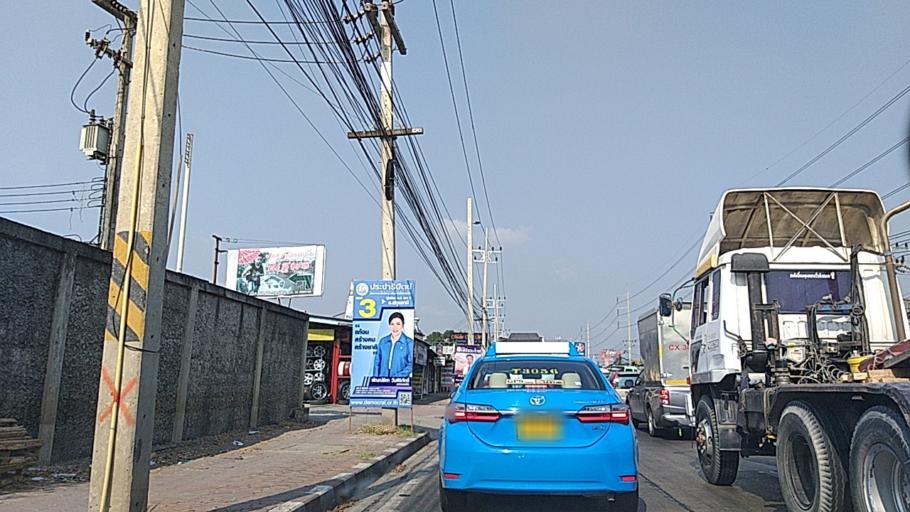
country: TH
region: Bangkok
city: Sai Mai
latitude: 13.9331
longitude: 100.6941
